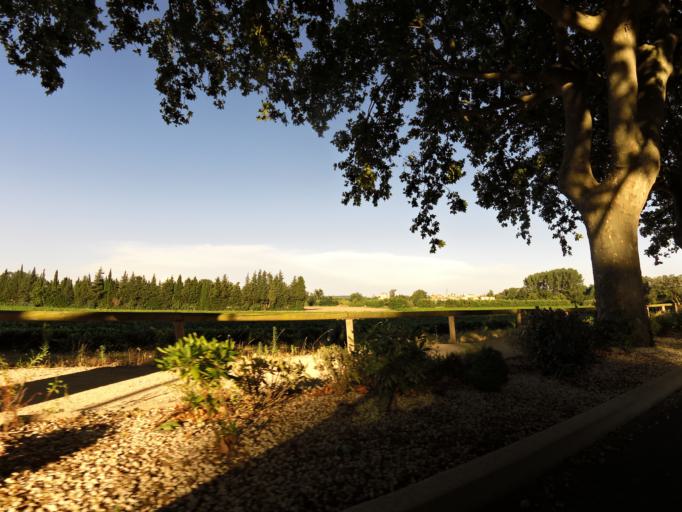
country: FR
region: Languedoc-Roussillon
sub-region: Departement du Gard
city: Remoulins
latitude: 43.9420
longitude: 4.5519
